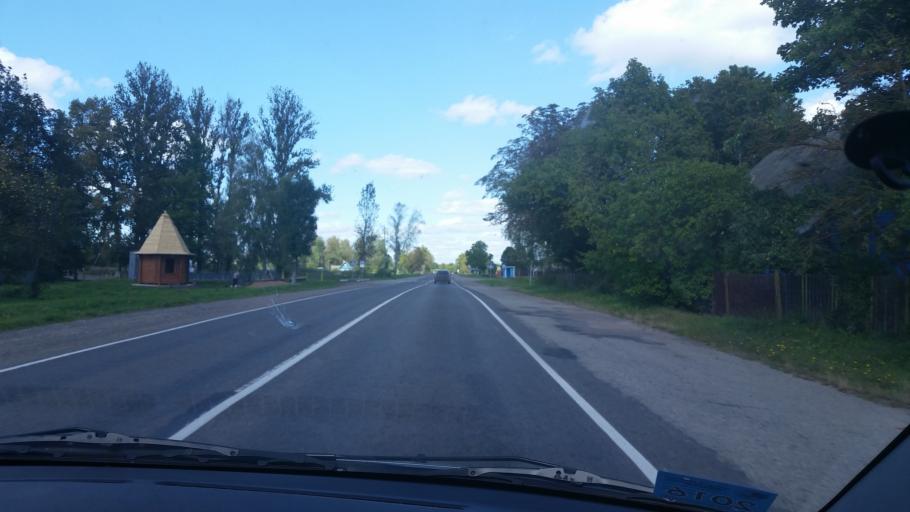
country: BY
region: Vitebsk
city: Vitebsk
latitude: 55.1110
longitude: 30.2829
